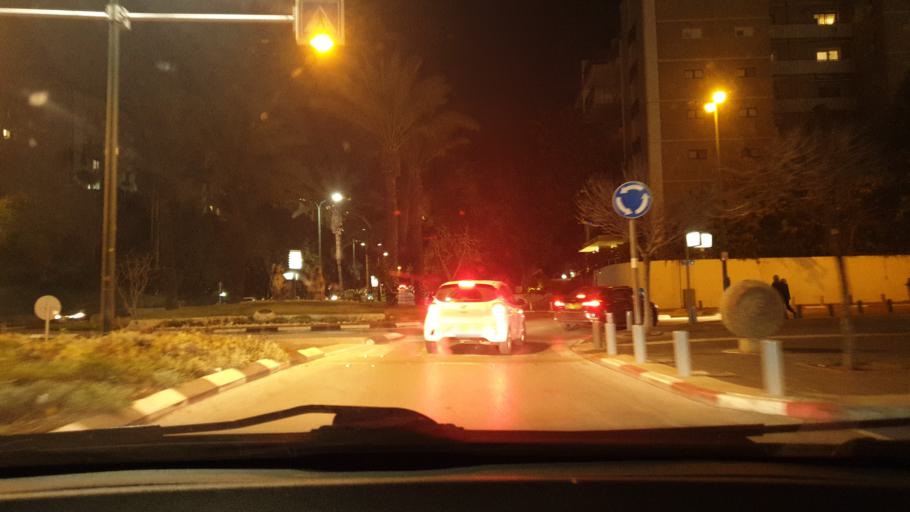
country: IL
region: Tel Aviv
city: Ramat Gan
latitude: 32.1249
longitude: 34.8012
